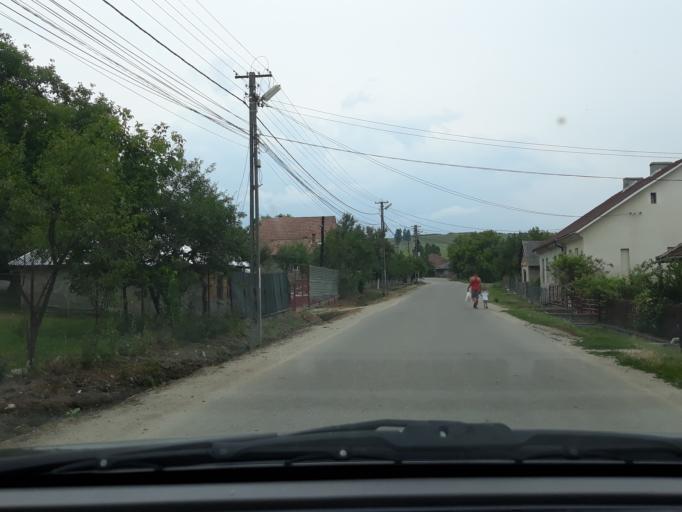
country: RO
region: Salaj
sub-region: Comuna Criseni
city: Criseni
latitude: 47.2544
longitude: 23.0647
